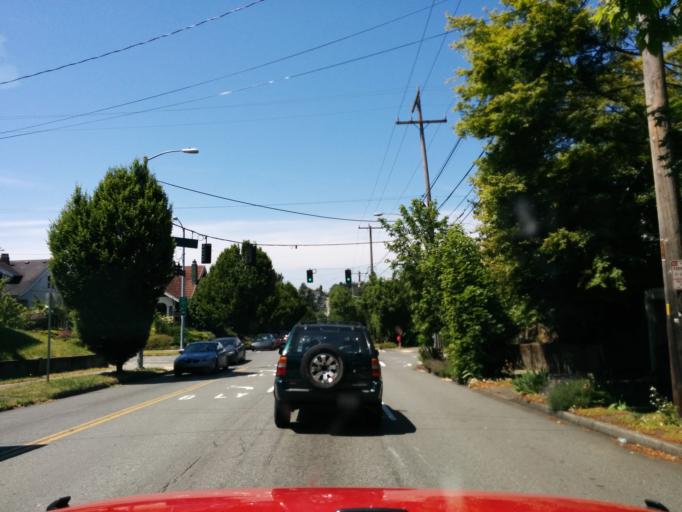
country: US
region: Washington
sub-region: King County
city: Seattle
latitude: 47.6650
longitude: -122.3358
